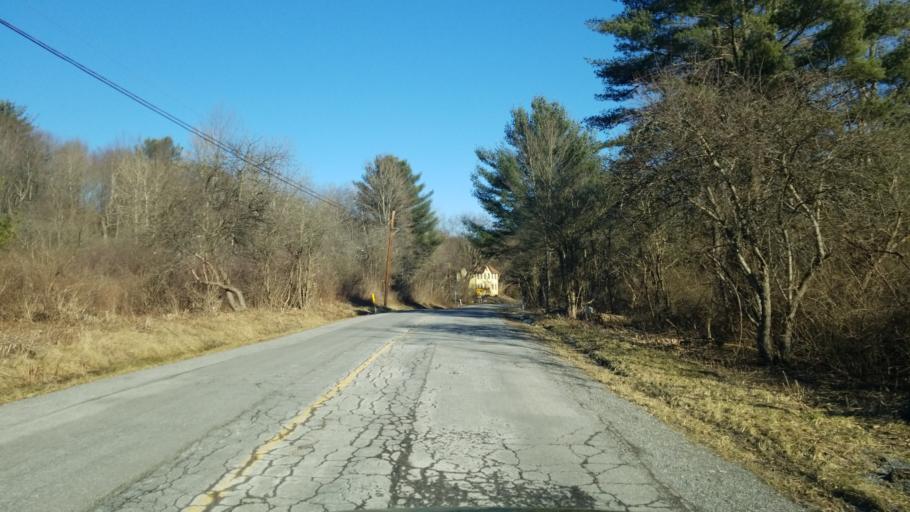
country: US
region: Pennsylvania
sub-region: Jefferson County
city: Sykesville
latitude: 41.0480
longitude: -78.7652
